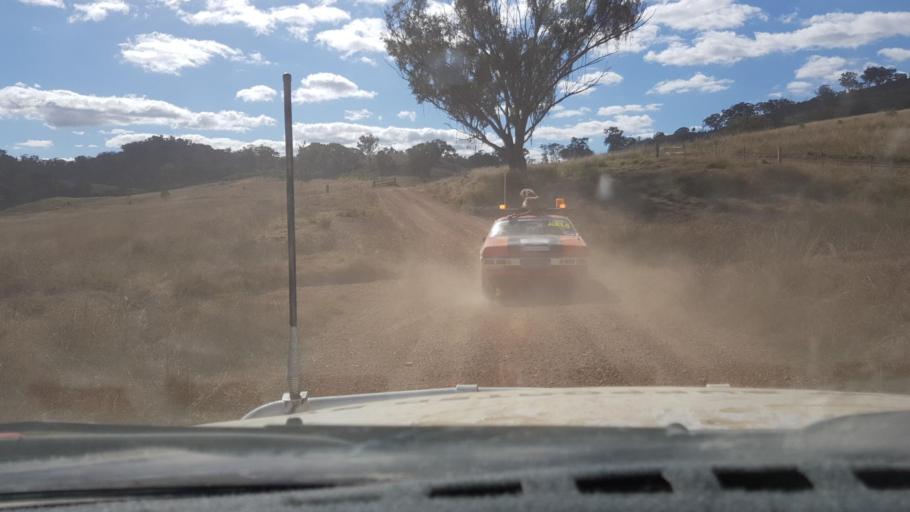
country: AU
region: New South Wales
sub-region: Tamworth Municipality
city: Manilla
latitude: -30.4406
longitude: 150.7874
